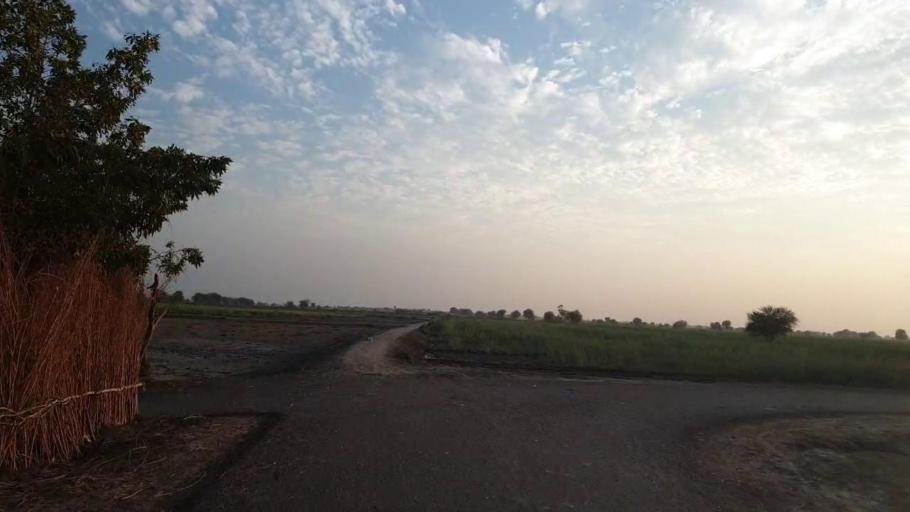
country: PK
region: Sindh
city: Pithoro
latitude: 25.5858
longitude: 69.3041
